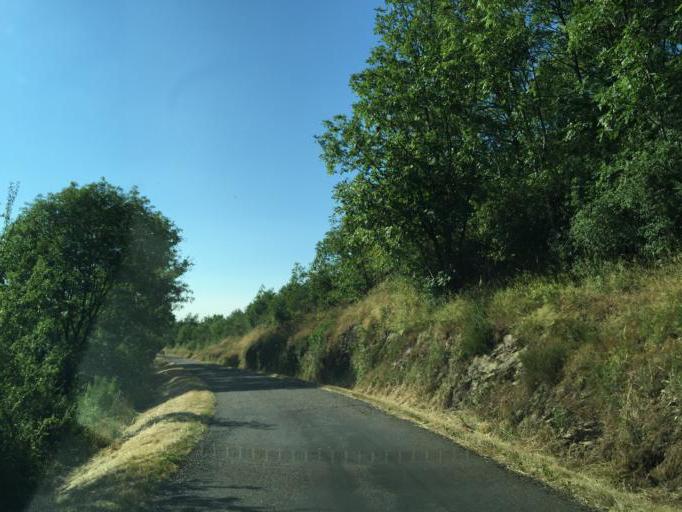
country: FR
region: Rhone-Alpes
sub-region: Departement de la Loire
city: Saint-Jean-Bonnefonds
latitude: 45.4351
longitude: 4.4895
